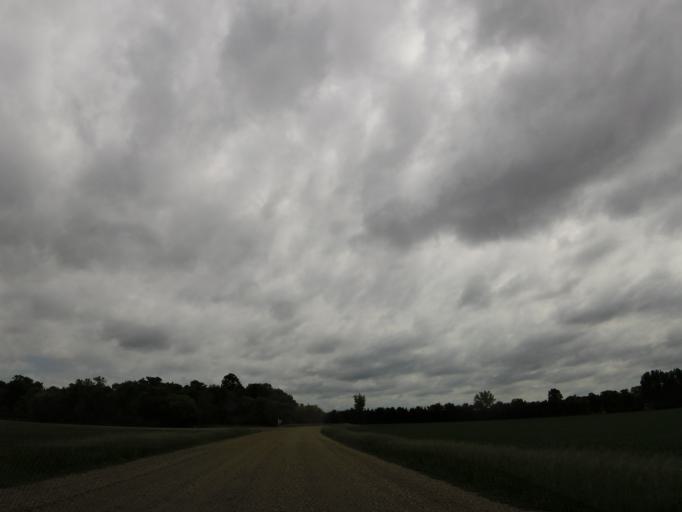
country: US
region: North Dakota
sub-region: Walsh County
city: Grafton
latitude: 48.4497
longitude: -97.4918
